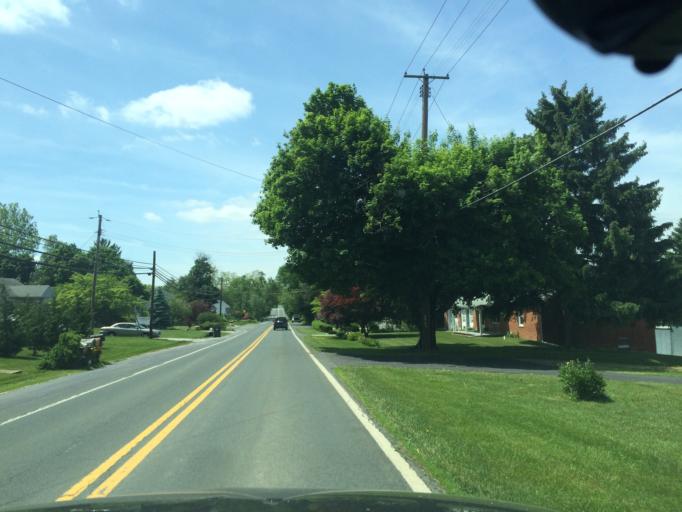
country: US
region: Maryland
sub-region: Carroll County
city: Westminster
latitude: 39.5497
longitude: -76.9525
